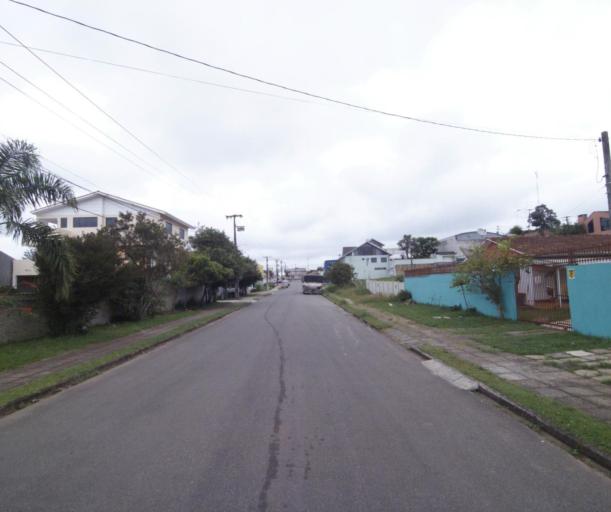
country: BR
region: Parana
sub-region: Quatro Barras
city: Quatro Barras
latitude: -25.3659
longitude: -49.1052
